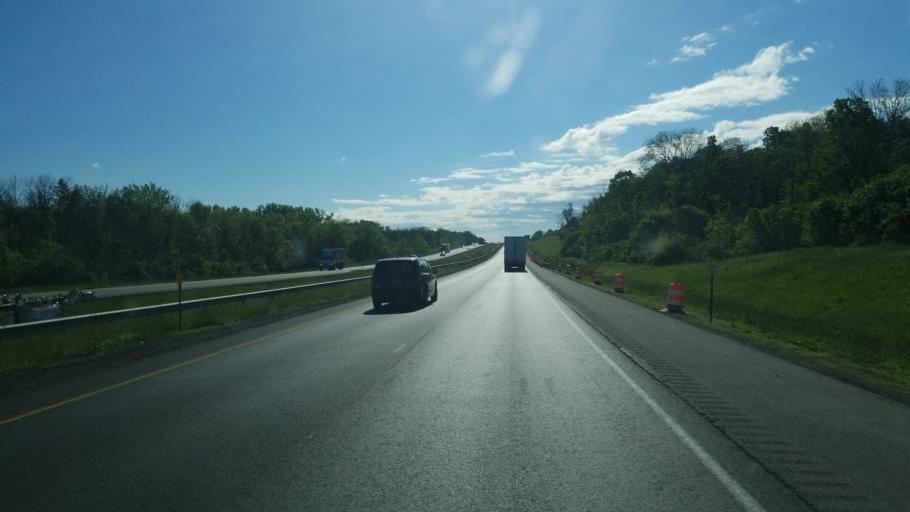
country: US
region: New York
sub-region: Livingston County
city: Caledonia
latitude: 43.0298
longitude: -77.8671
